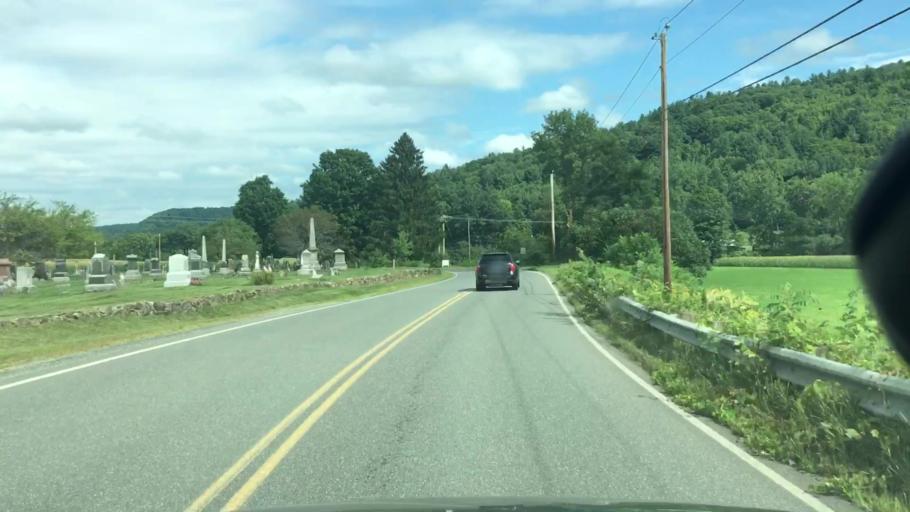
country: US
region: Massachusetts
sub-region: Franklin County
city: Colrain
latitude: 42.6849
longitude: -72.6911
